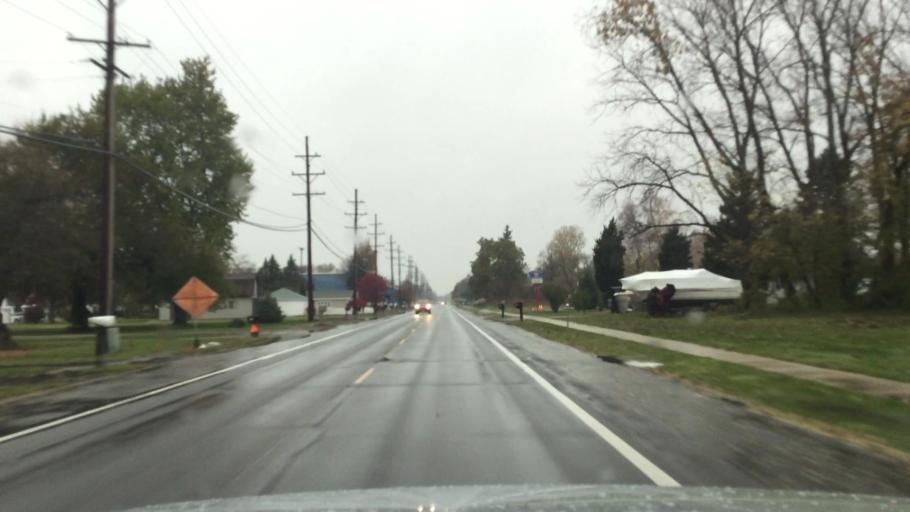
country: US
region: Michigan
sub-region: Saint Clair County
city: Pearl Beach
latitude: 42.6241
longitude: -82.5897
